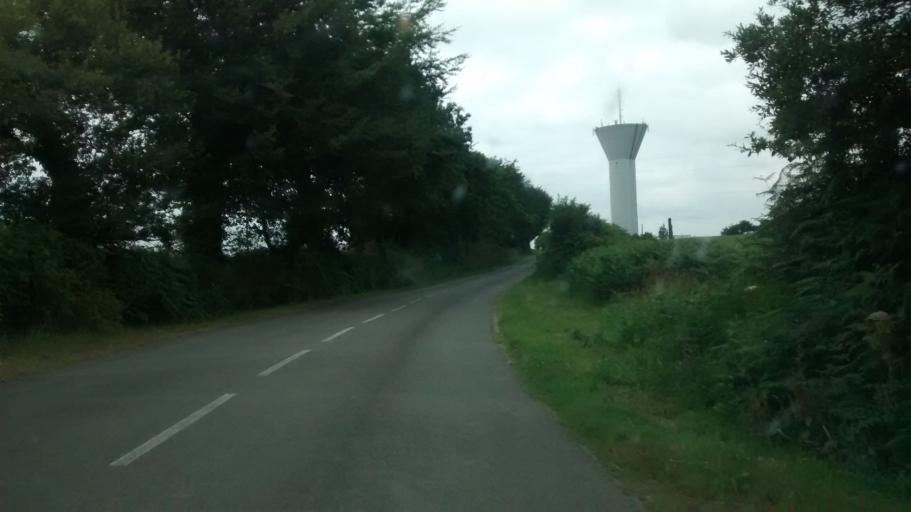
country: FR
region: Brittany
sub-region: Departement du Finistere
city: Plouedern
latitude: 48.4805
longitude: -4.2595
